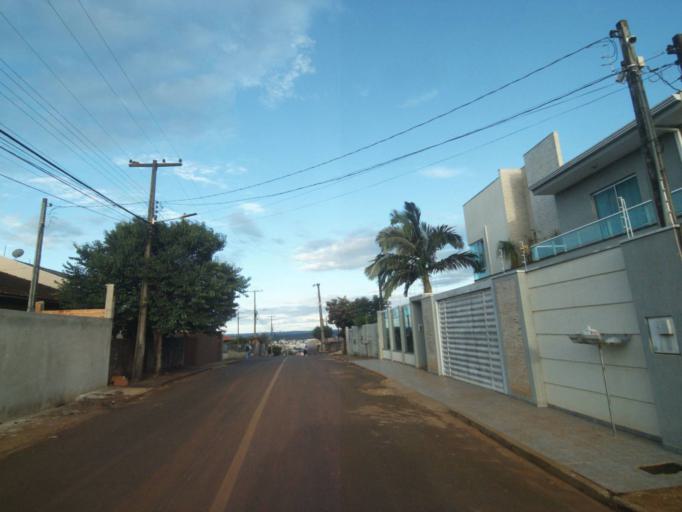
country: BR
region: Parana
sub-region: Telemaco Borba
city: Telemaco Borba
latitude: -24.3285
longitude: -50.6414
